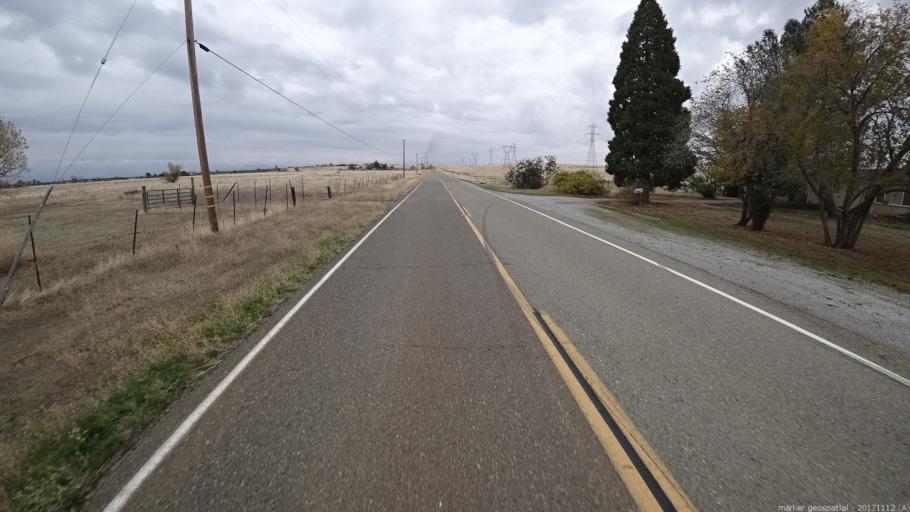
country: US
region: California
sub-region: Shasta County
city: Palo Cedro
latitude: 40.4915
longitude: -122.2026
